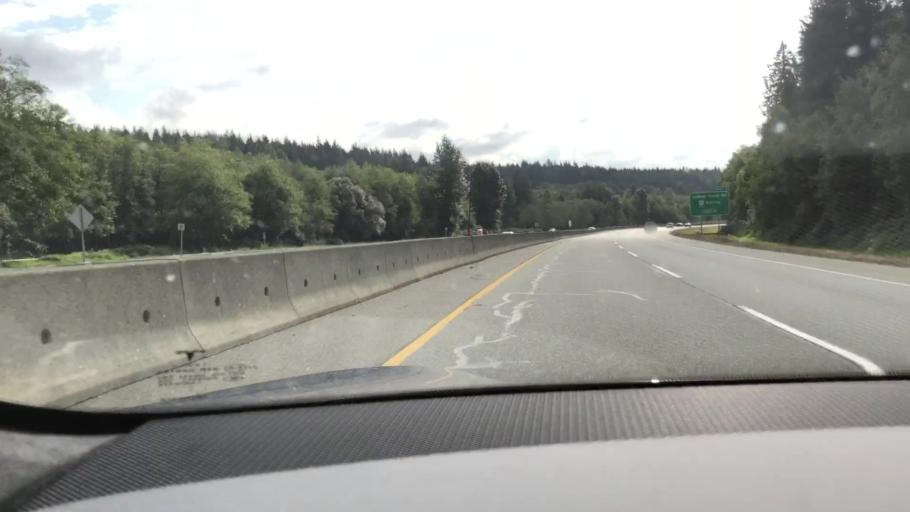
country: CA
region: British Columbia
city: Delta
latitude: 49.1138
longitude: -122.9129
